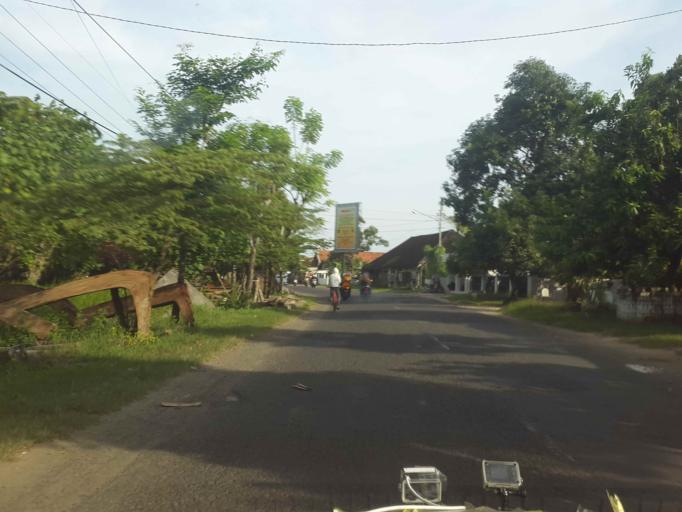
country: ID
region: East Java
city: Pasarkayu
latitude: -7.0278
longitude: 113.8824
